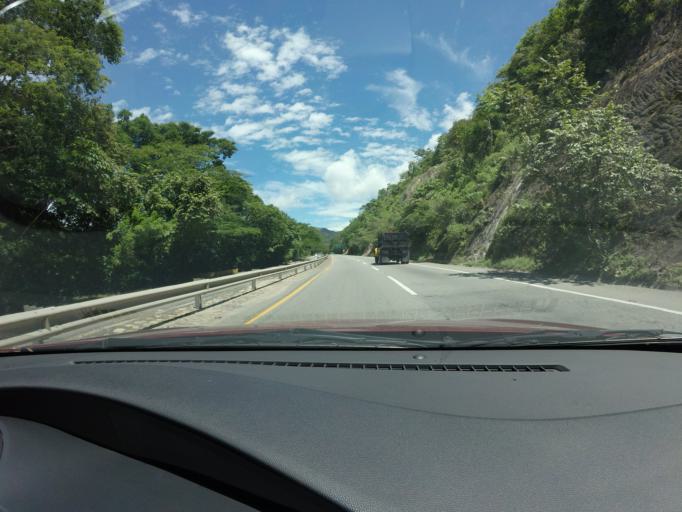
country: CO
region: Cundinamarca
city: Ricaurte
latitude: 4.2480
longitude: -74.7363
